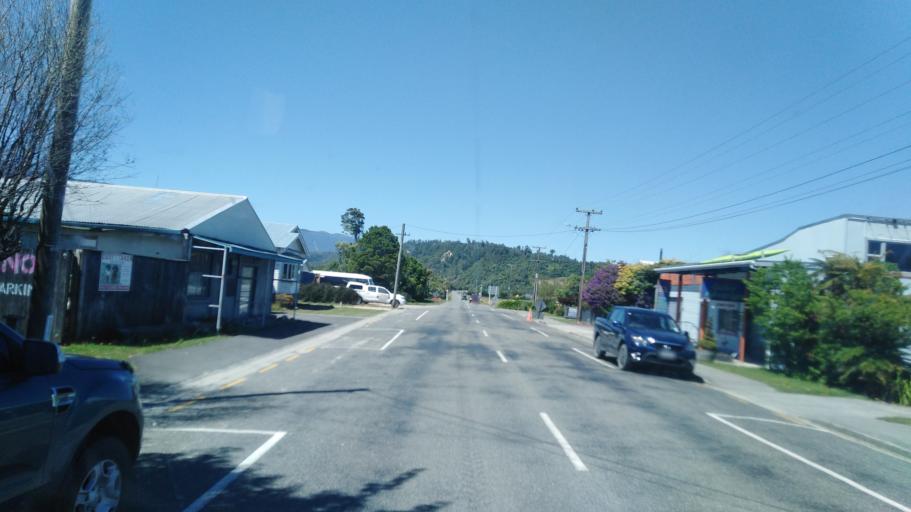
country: NZ
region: West Coast
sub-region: Buller District
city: Westport
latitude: -41.2520
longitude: 172.1289
